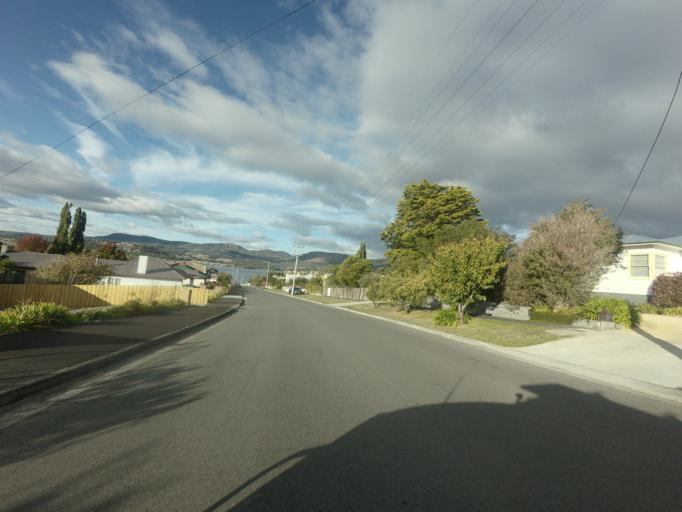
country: AU
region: Tasmania
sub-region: Glenorchy
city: Claremont
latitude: -42.7866
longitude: 147.2485
